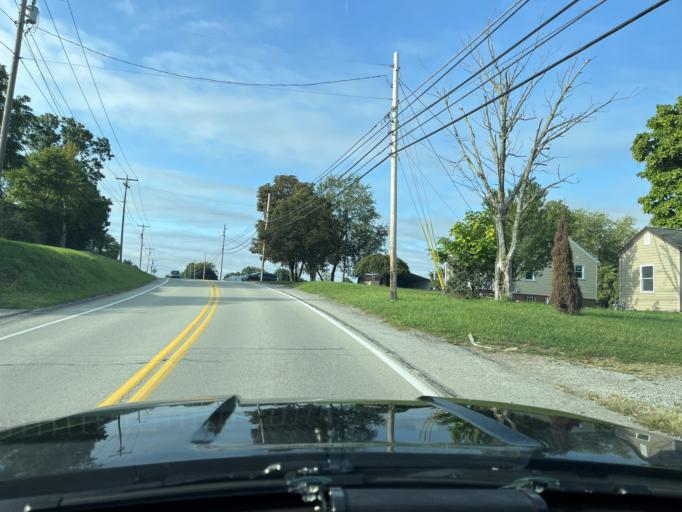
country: US
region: Pennsylvania
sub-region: Fayette County
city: Leith-Hatfield
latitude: 39.8763
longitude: -79.7404
